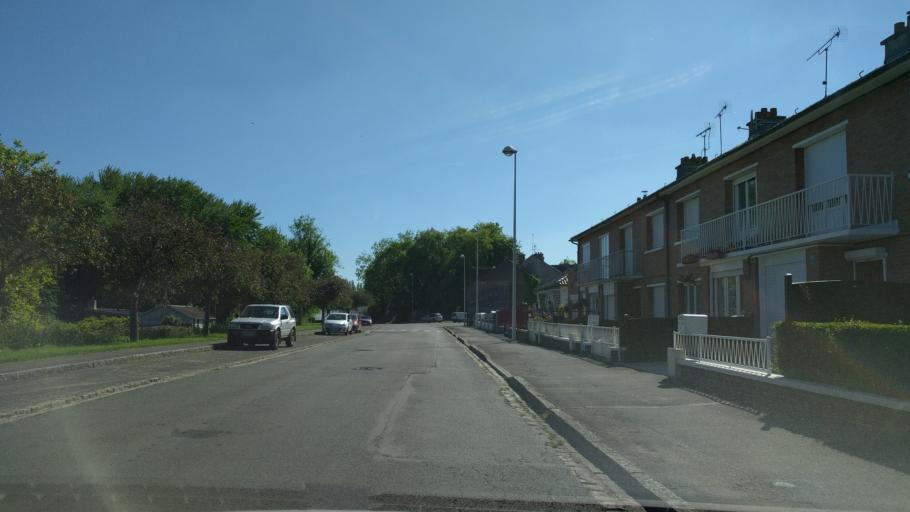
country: FR
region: Picardie
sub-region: Departement de la Somme
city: Peronne
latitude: 49.9252
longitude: 2.9328
